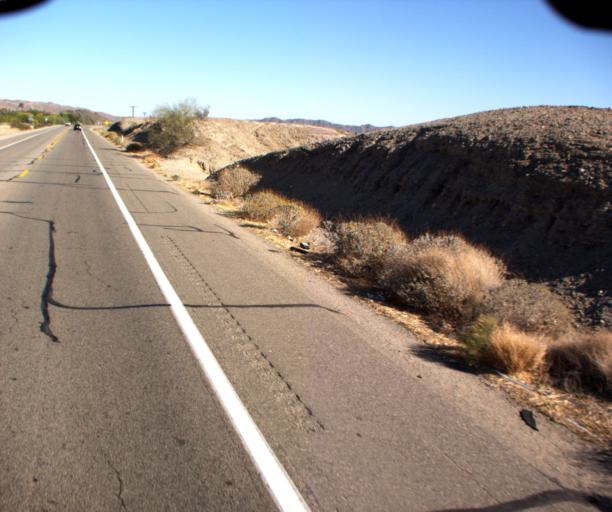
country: US
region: Arizona
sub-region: Yuma County
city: Fortuna Foothills
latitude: 32.7351
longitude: -114.4243
